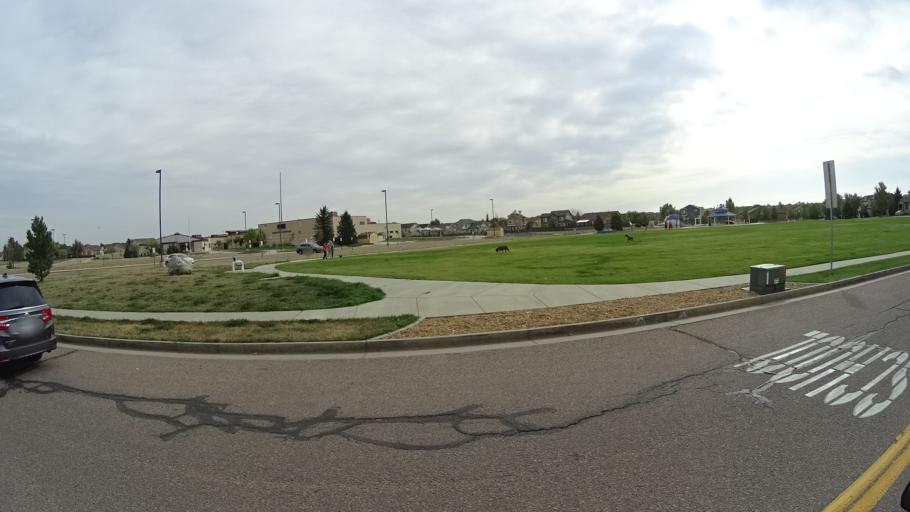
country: US
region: Colorado
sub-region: El Paso County
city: Cimarron Hills
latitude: 38.9207
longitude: -104.7012
